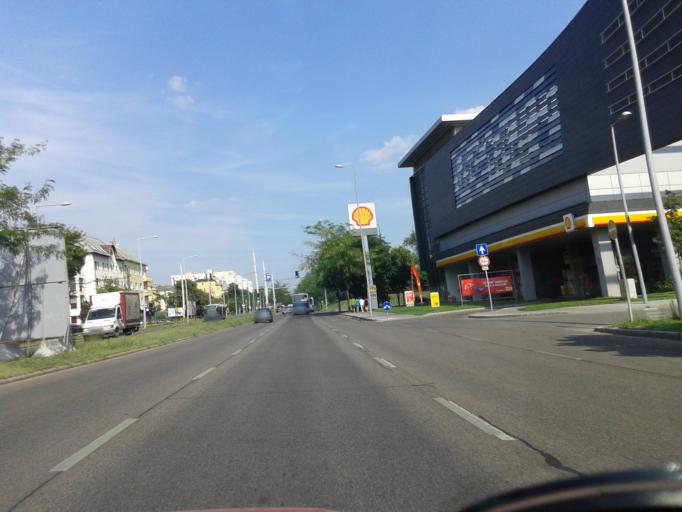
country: HU
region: Budapest
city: Budapest X. keruelet
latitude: 47.5036
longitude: 19.1403
